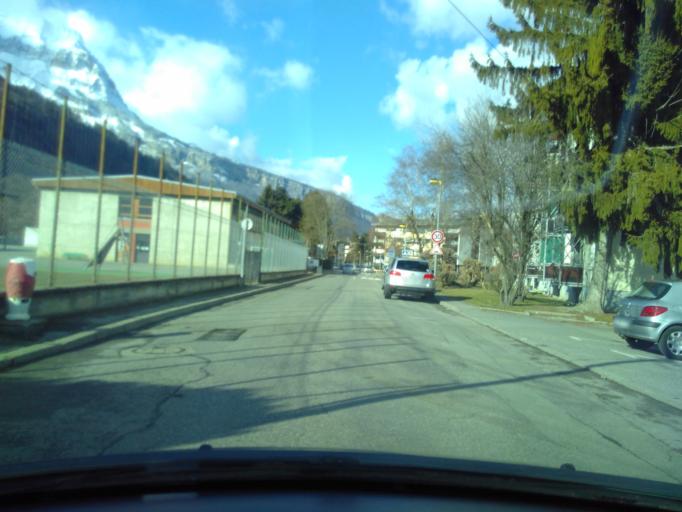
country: FR
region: Rhone-Alpes
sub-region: Departement de la Haute-Savoie
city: Sallanches
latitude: 45.9432
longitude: 6.6328
